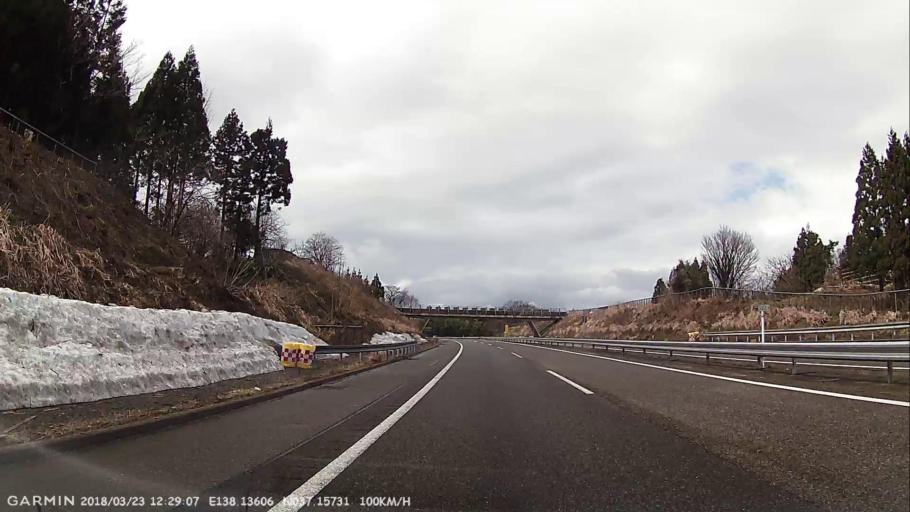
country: JP
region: Niigata
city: Joetsu
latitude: 37.1573
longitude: 138.1360
